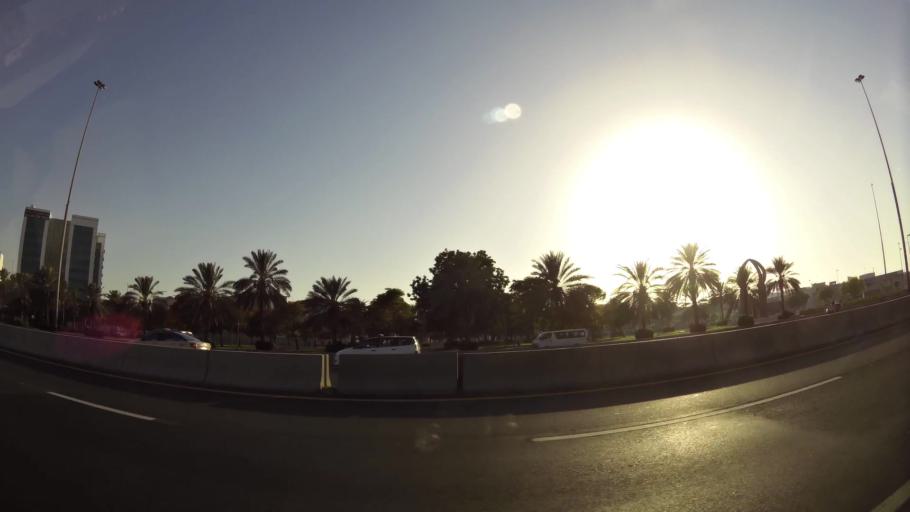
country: AE
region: Ash Shariqah
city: Sharjah
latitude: 25.2620
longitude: 55.3368
